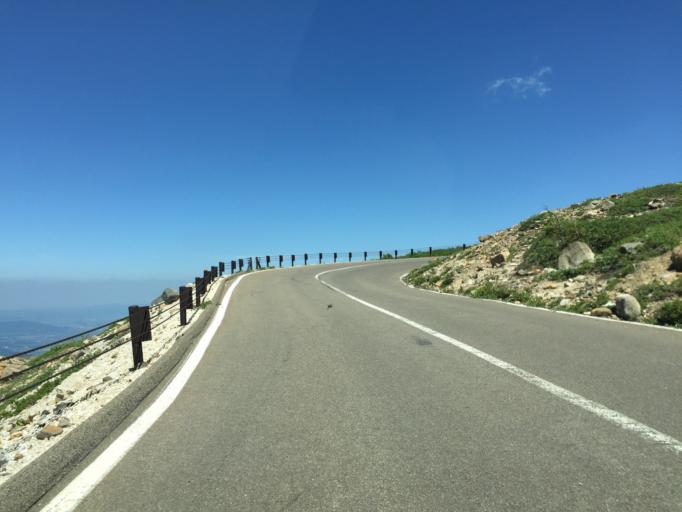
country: JP
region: Fukushima
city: Fukushima-shi
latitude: 37.7261
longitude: 140.2589
